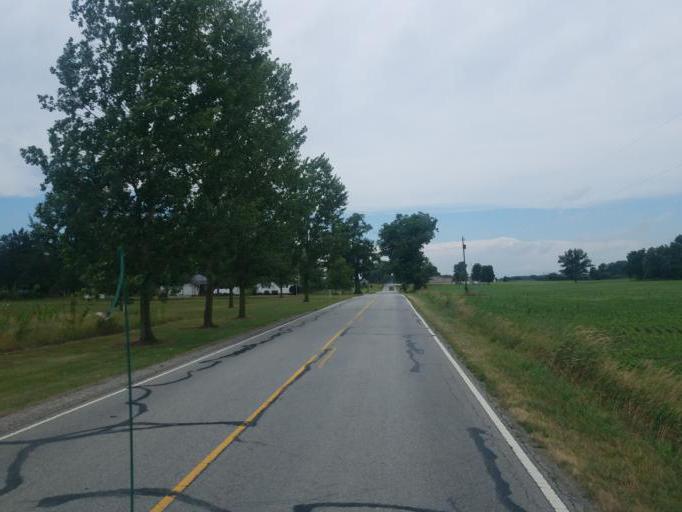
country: US
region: Indiana
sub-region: DeKalb County
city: Butler
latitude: 41.3861
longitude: -84.8516
